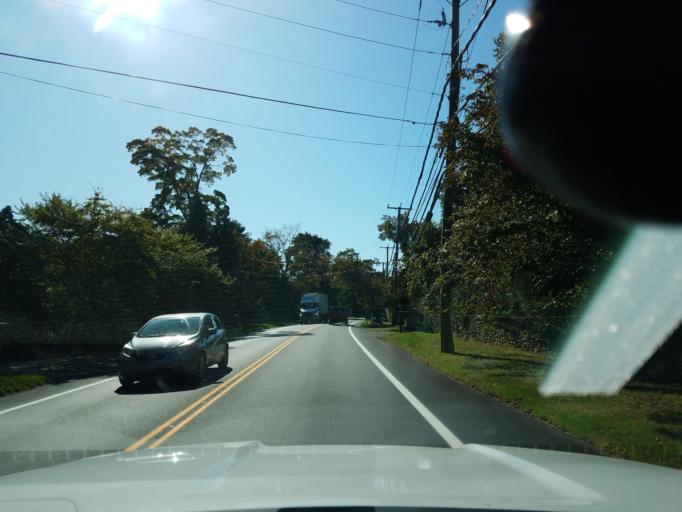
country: US
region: Connecticut
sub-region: Fairfield County
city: Cos Cob
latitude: 41.0554
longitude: -73.6168
